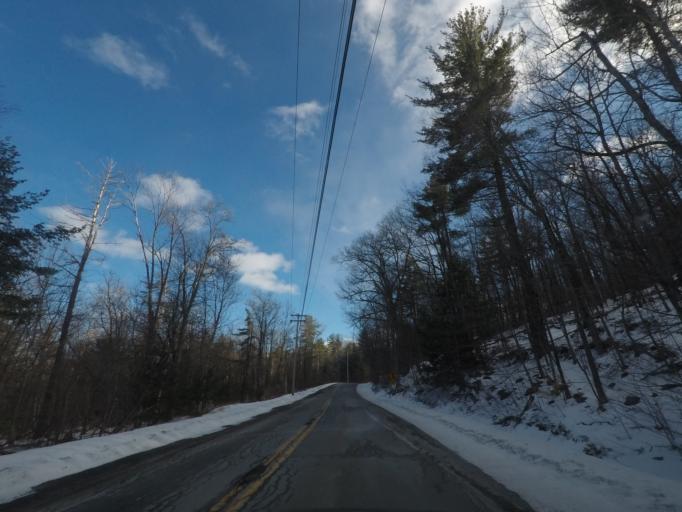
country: US
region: New York
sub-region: Rensselaer County
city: Hoosick Falls
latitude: 42.8159
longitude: -73.3915
